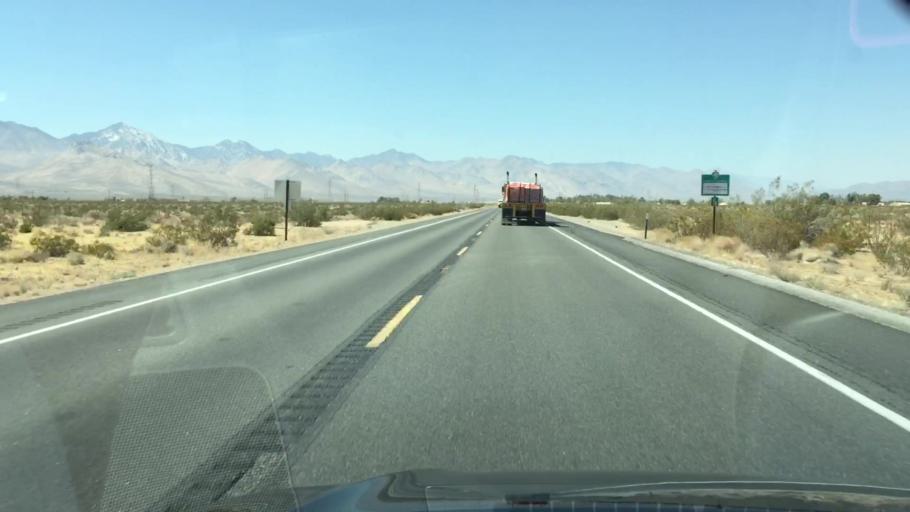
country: US
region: California
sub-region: Kern County
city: China Lake Acres
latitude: 35.6264
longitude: -117.7790
